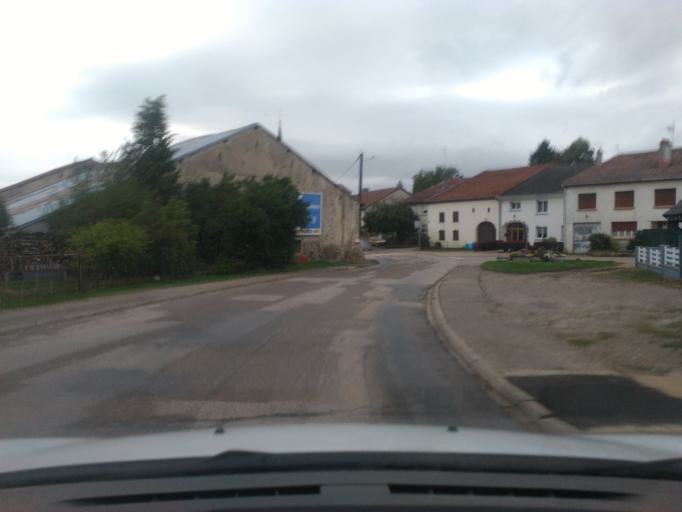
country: FR
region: Lorraine
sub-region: Departement des Vosges
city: Chatel-sur-Moselle
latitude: 48.3466
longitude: 6.4354
